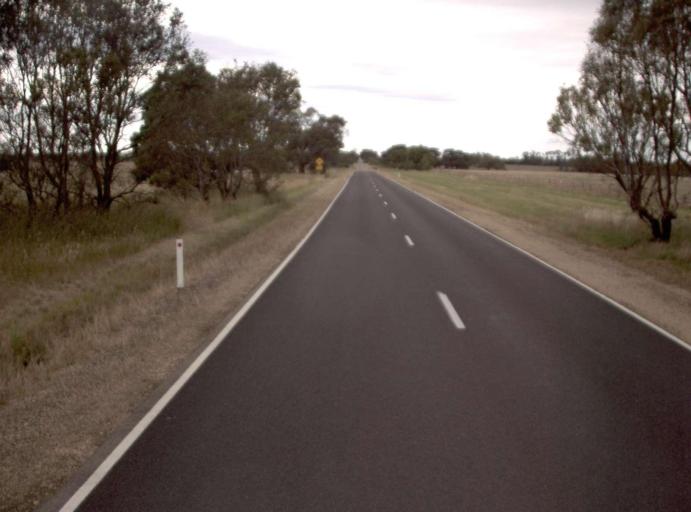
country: AU
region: Victoria
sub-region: Wellington
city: Sale
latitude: -38.0002
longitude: 147.2186
